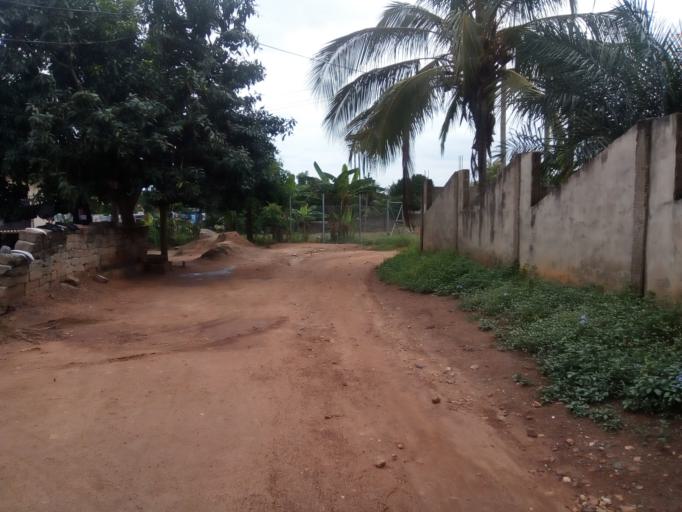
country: GH
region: Eastern
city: Nsawam
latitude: 5.7804
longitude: -0.3384
